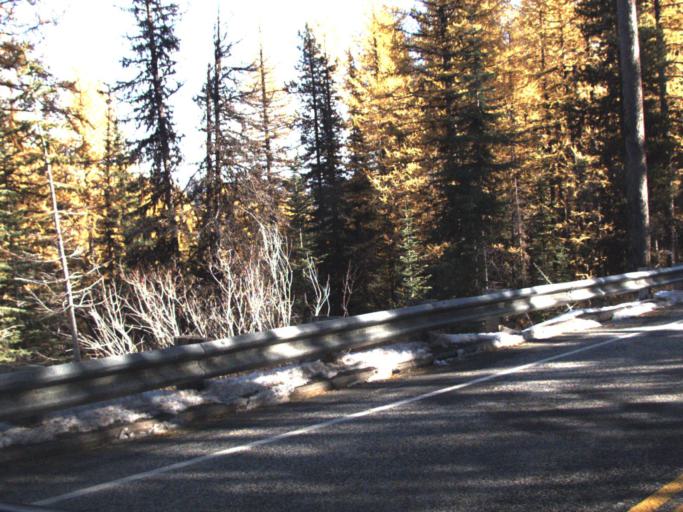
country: US
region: Washington
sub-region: Ferry County
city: Republic
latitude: 48.6066
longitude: -118.4757
